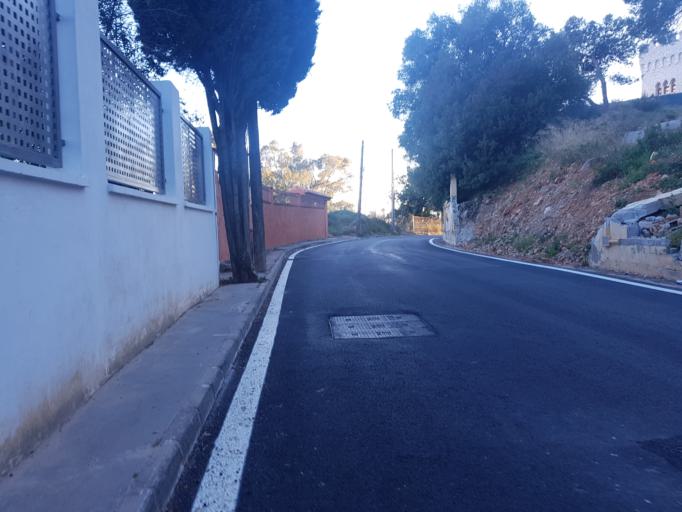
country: ES
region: Andalusia
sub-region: Provincia de Malaga
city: Marbella
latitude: 36.5281
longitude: -4.8855
